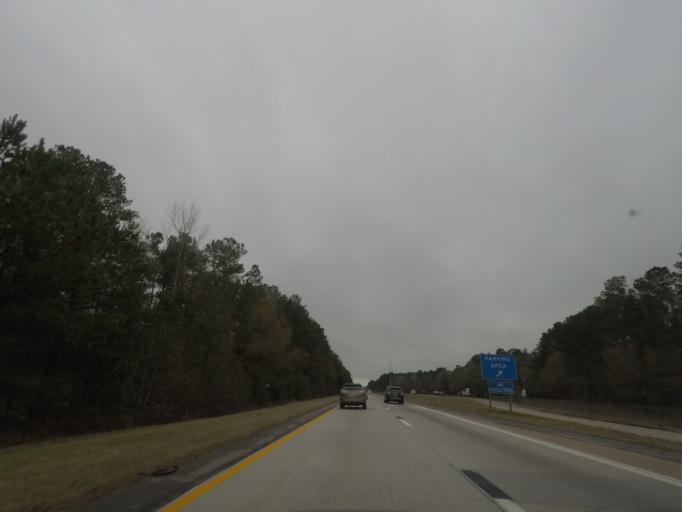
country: US
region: South Carolina
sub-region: Dorchester County
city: Saint George
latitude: 33.1621
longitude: -80.6205
